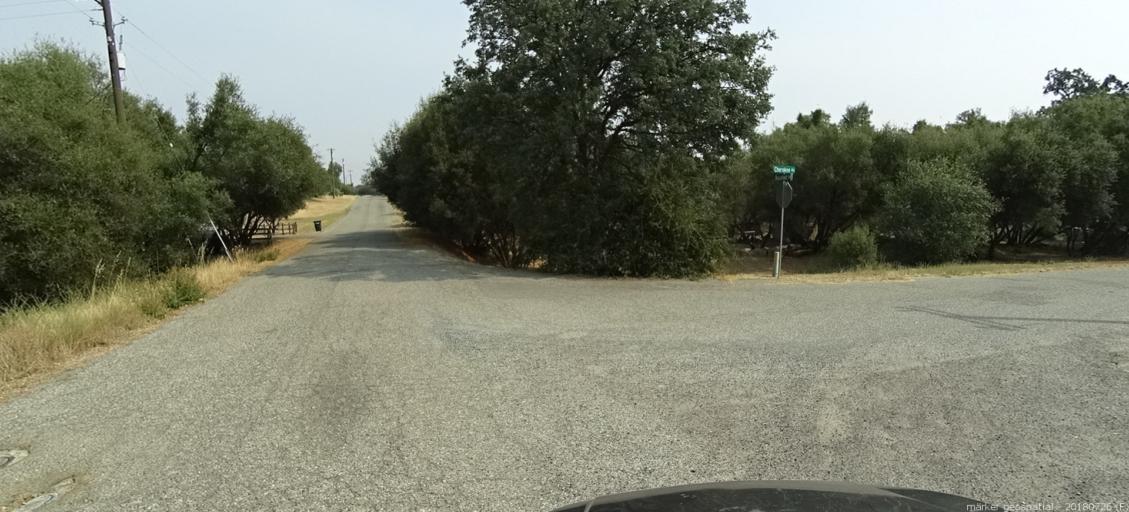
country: US
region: California
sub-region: Madera County
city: Coarsegold
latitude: 37.2061
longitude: -119.6823
